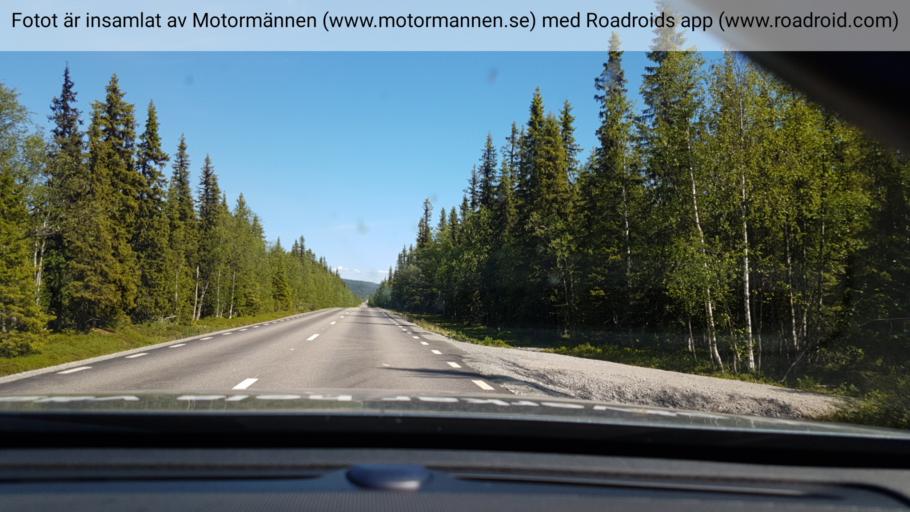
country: SE
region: Vaesterbotten
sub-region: Asele Kommun
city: Insjon
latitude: 64.7264
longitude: 17.5764
